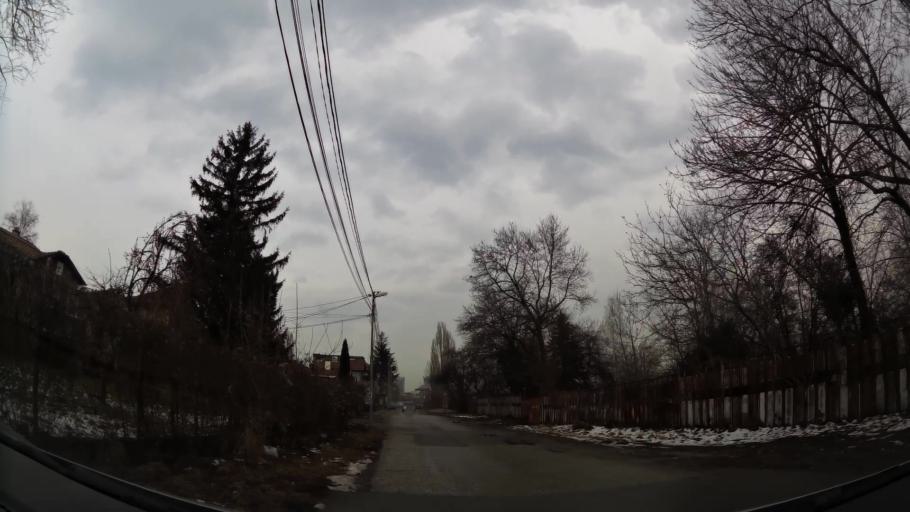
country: BG
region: Sofia-Capital
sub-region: Stolichna Obshtina
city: Sofia
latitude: 42.6655
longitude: 23.2471
